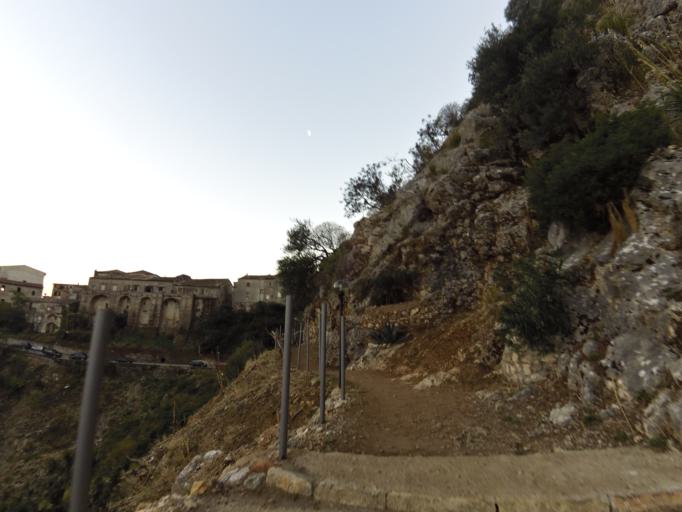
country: IT
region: Calabria
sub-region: Provincia di Reggio Calabria
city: Stilo
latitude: 38.4815
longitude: 16.4692
